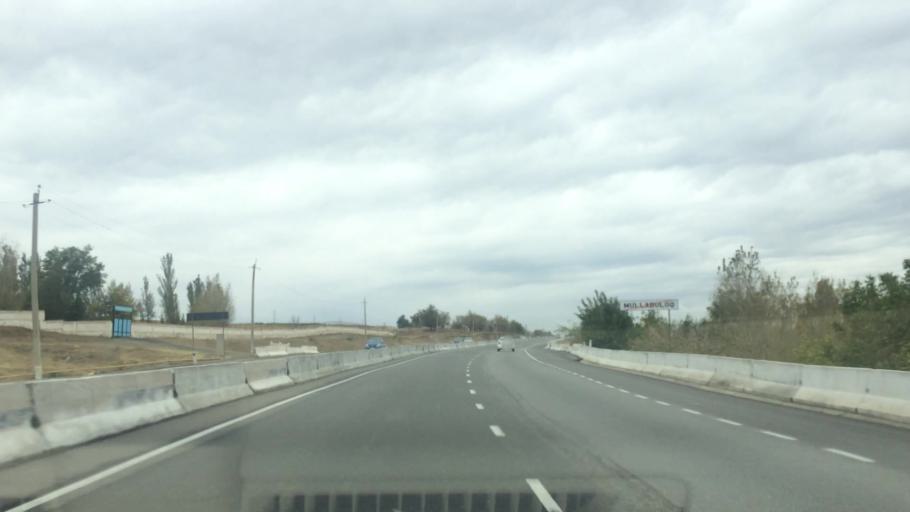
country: UZ
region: Samarqand
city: Bulung'ur
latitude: 39.9491
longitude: 67.5364
